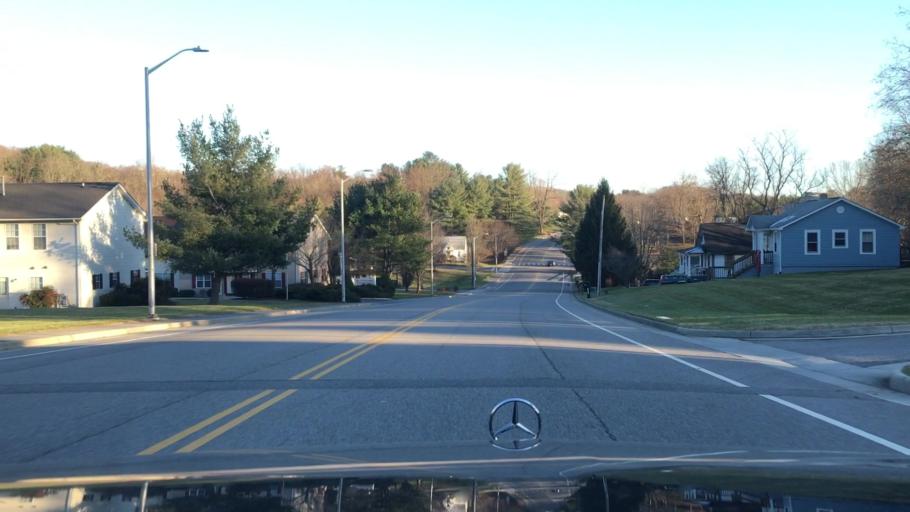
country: US
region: Virginia
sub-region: Montgomery County
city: Blacksburg
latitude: 37.2460
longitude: -80.4142
